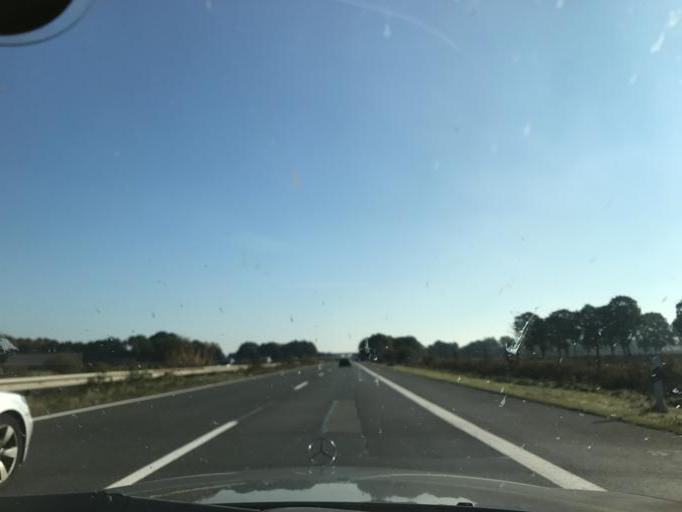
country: DE
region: Lower Saxony
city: Wiefelstede
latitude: 53.1856
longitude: 8.1064
